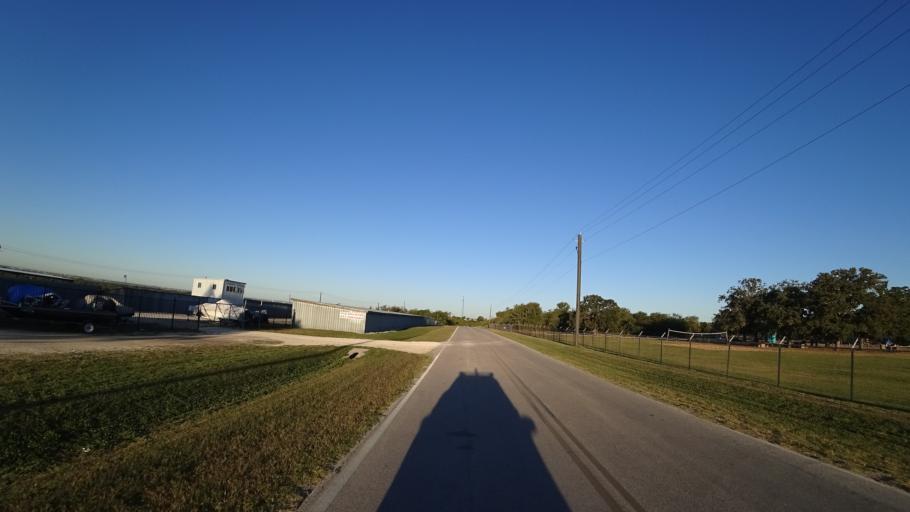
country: US
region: Texas
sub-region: Travis County
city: Hornsby Bend
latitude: 30.2818
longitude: -97.6099
